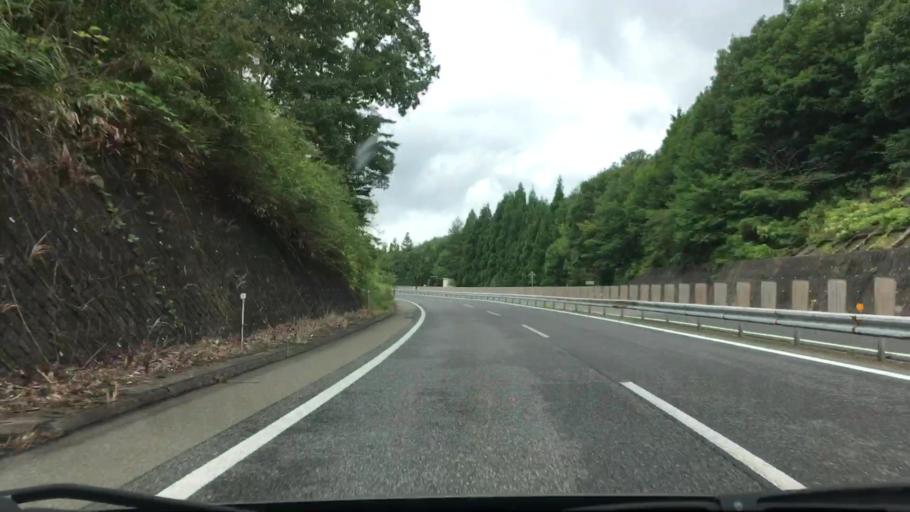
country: JP
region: Hiroshima
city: Shobara
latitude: 34.8944
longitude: 133.2121
